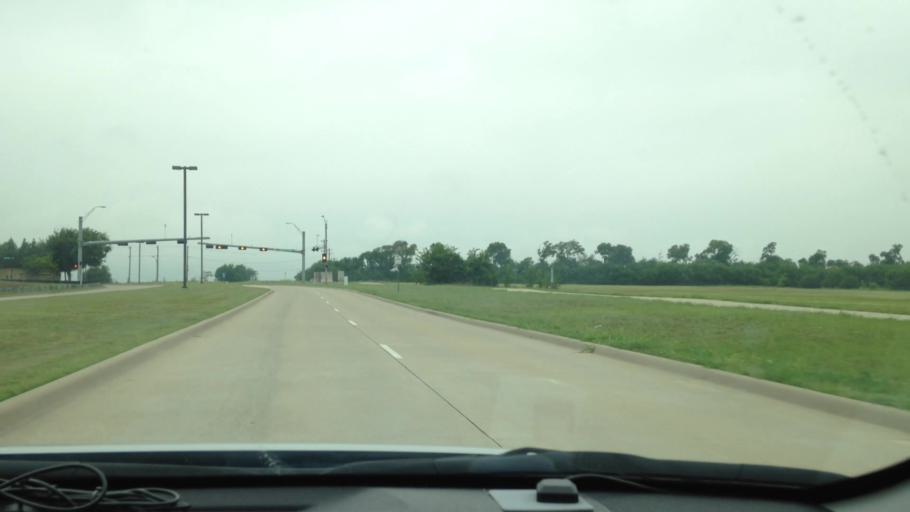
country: US
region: Texas
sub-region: Collin County
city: Allen
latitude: 33.1231
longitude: -96.7208
